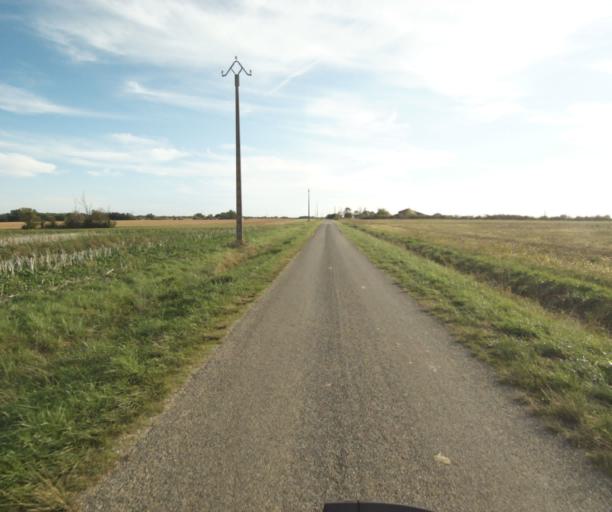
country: FR
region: Midi-Pyrenees
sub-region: Departement du Tarn-et-Garonne
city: Finhan
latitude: 43.9156
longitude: 1.1316
